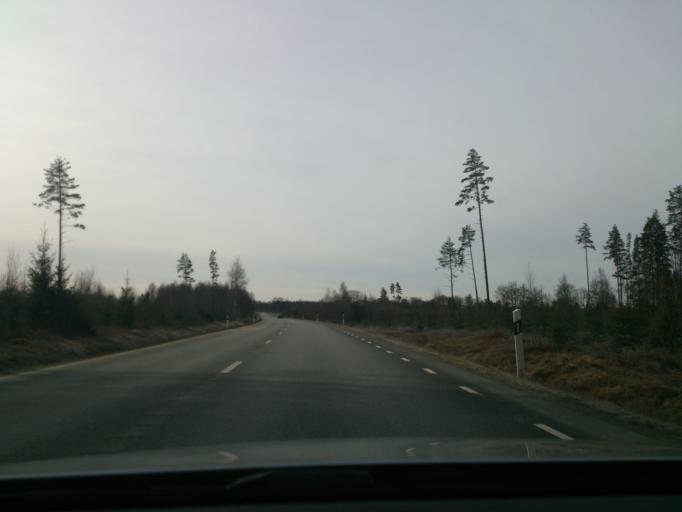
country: SE
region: Kronoberg
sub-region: Alvesta Kommun
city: Alvesta
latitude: 56.9428
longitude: 14.5608
